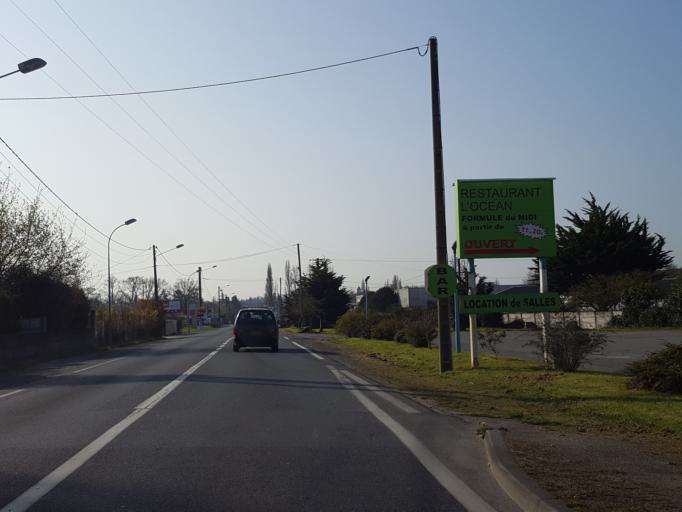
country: FR
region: Pays de la Loire
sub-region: Departement de la Loire-Atlantique
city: Geneston
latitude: 47.0655
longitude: -1.5177
